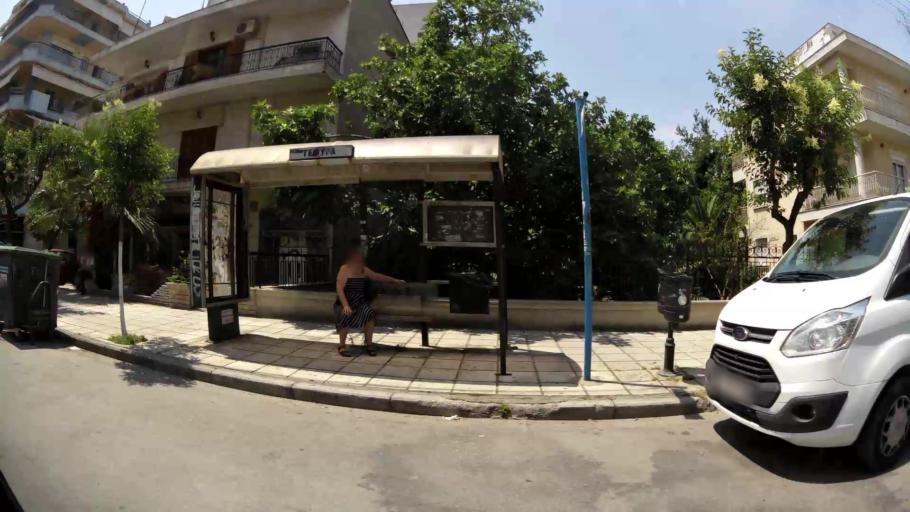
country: GR
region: Central Macedonia
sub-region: Nomos Thessalonikis
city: Ampelokipoi
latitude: 40.6573
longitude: 22.9264
